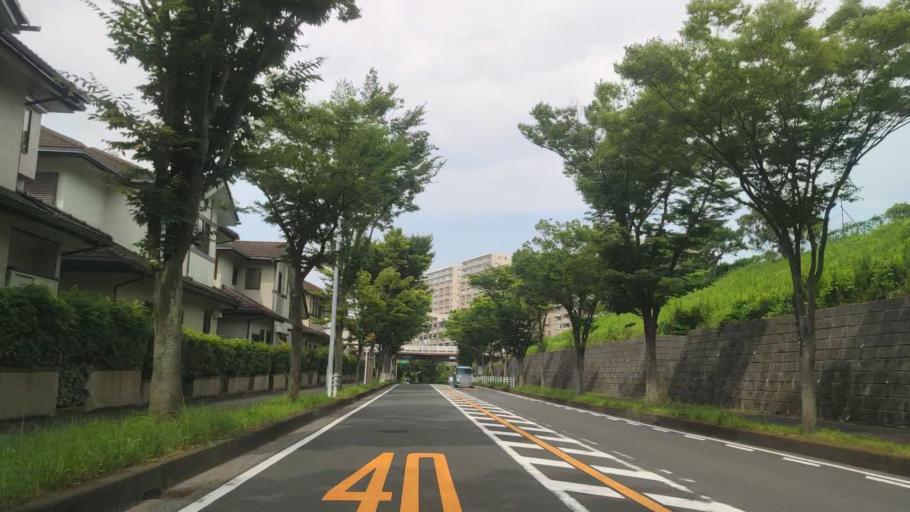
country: JP
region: Kanagawa
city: Zushi
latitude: 35.3535
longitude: 139.6207
